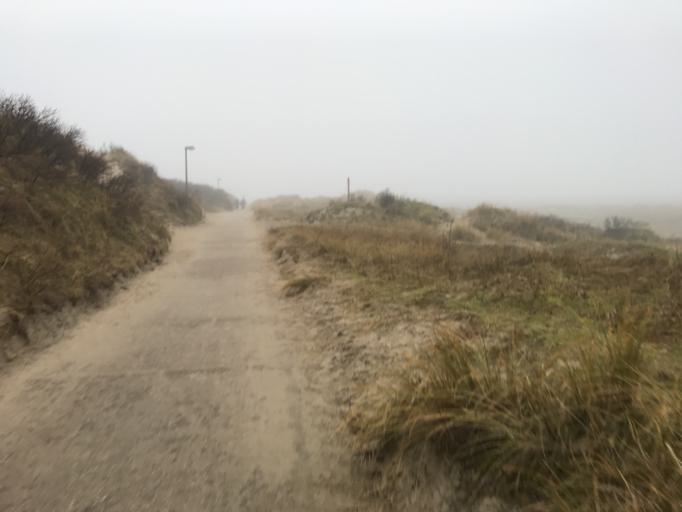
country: DE
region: Lower Saxony
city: Borkum
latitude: 53.5984
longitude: 6.6681
